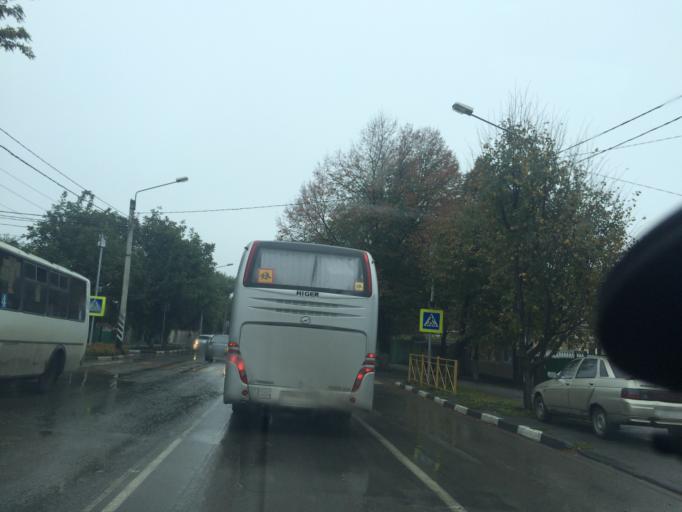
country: RU
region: Rostov
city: Azov
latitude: 47.0936
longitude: 39.4493
